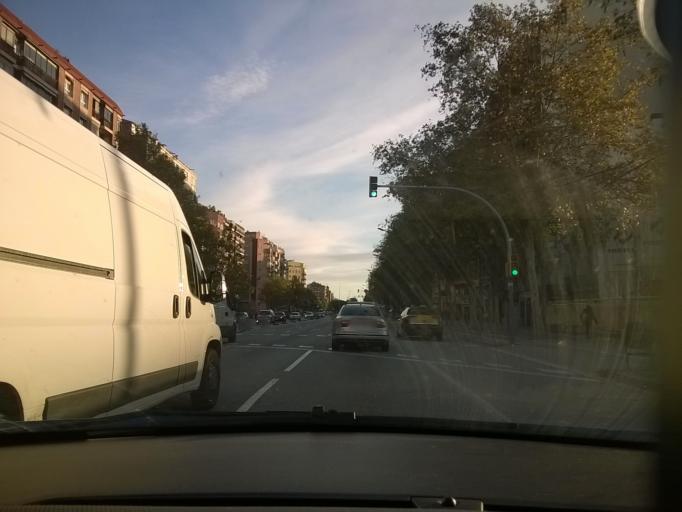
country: ES
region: Catalonia
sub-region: Provincia de Barcelona
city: Sant Marti
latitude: 41.4135
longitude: 2.1869
